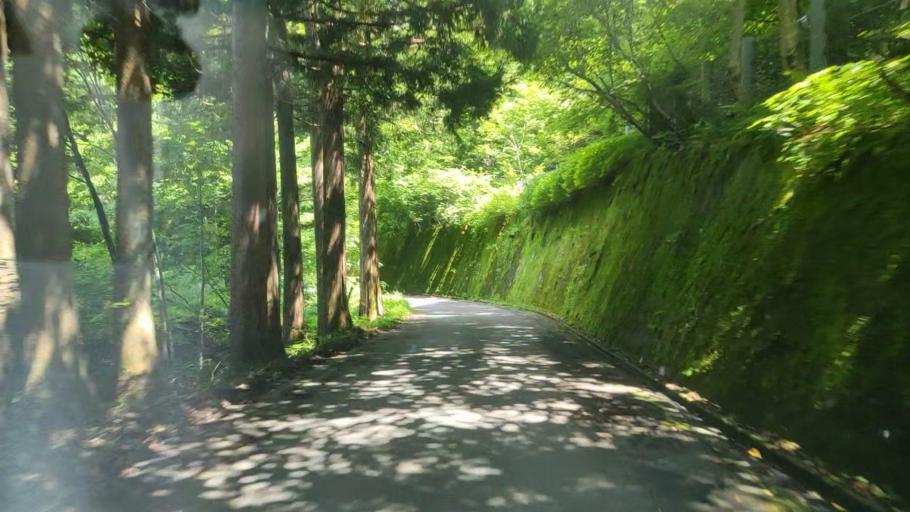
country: JP
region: Fukui
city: Ono
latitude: 35.7569
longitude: 136.5695
